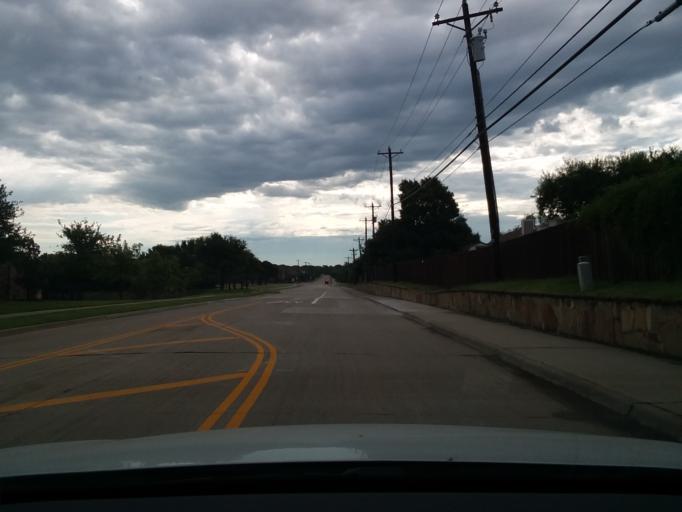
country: US
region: Texas
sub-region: Denton County
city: Highland Village
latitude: 33.0606
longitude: -97.0546
